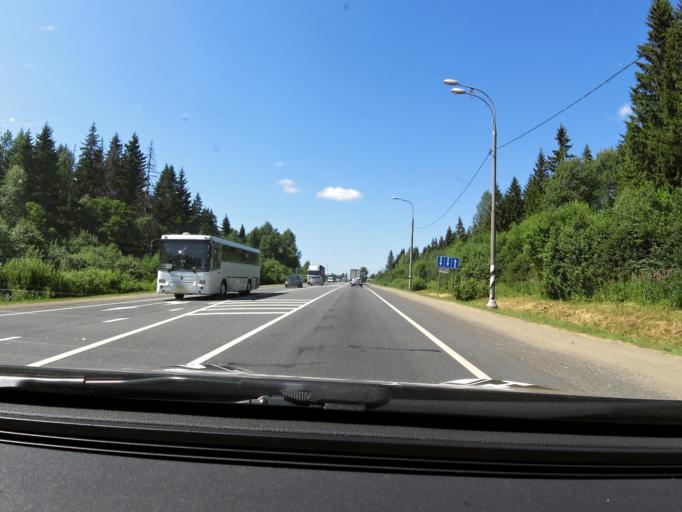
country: RU
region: Novgorod
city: Kresttsy
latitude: 58.0939
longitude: 32.8629
